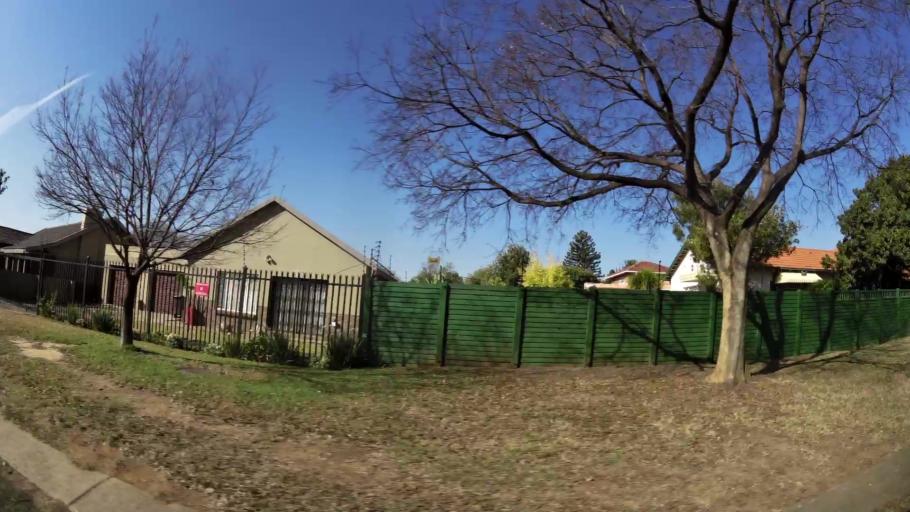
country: ZA
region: Gauteng
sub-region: City of Tshwane Metropolitan Municipality
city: Pretoria
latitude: -25.7285
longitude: 28.2547
